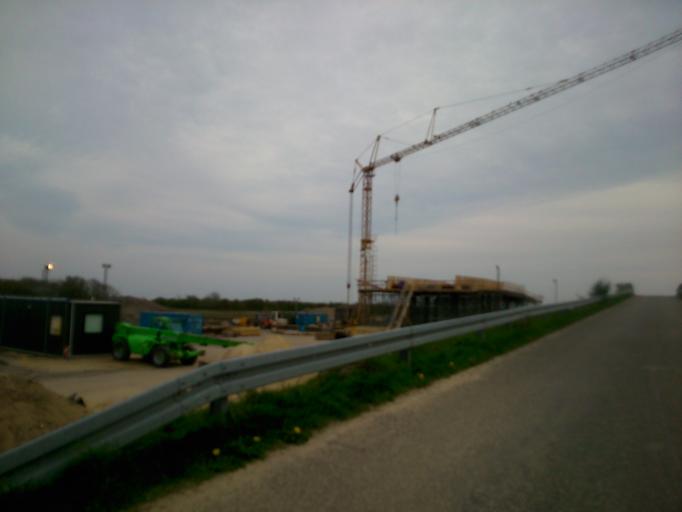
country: DK
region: South Denmark
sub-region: Esbjerg Kommune
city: Bramming
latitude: 55.4666
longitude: 8.6519
